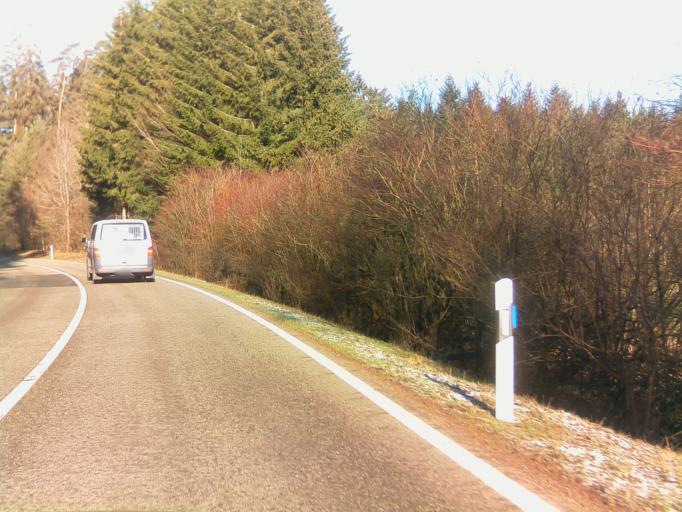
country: DE
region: Baden-Wuerttemberg
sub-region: Karlsruhe Region
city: Oberreichenbach
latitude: 48.7279
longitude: 8.6551
